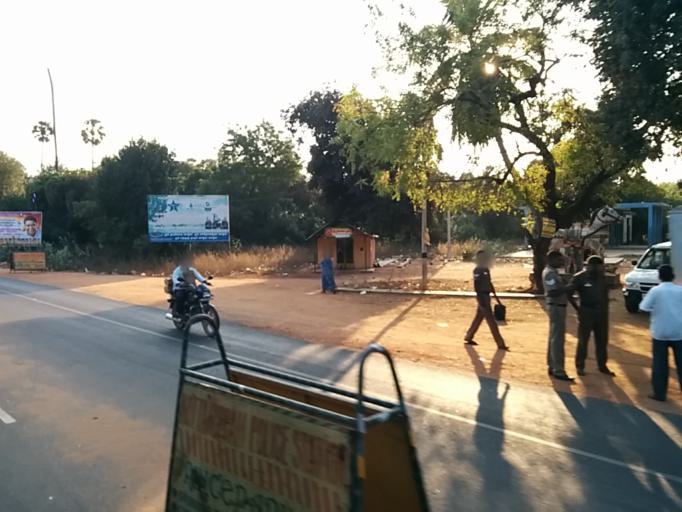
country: IN
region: Tamil Nadu
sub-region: Villupuram
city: Auroville
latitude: 11.9826
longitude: 79.8450
